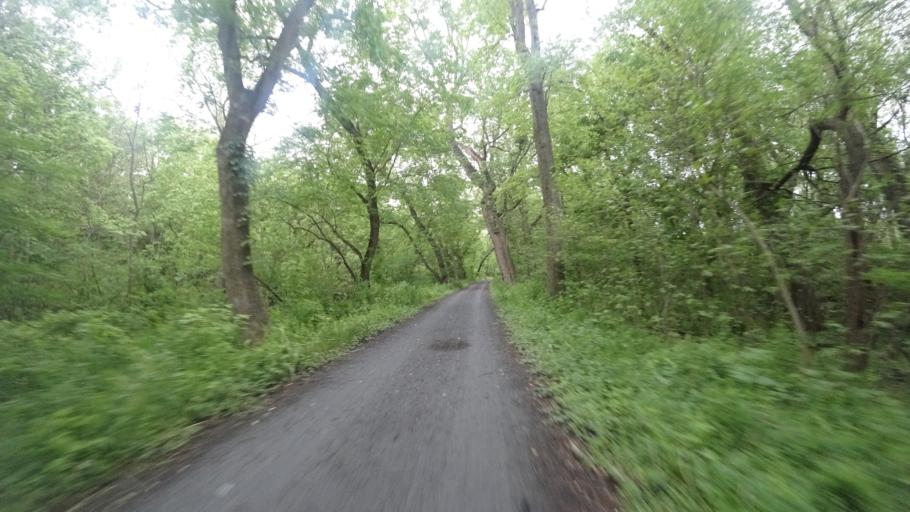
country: US
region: Maryland
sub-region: Frederick County
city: Brunswick
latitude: 39.3285
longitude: -77.6710
